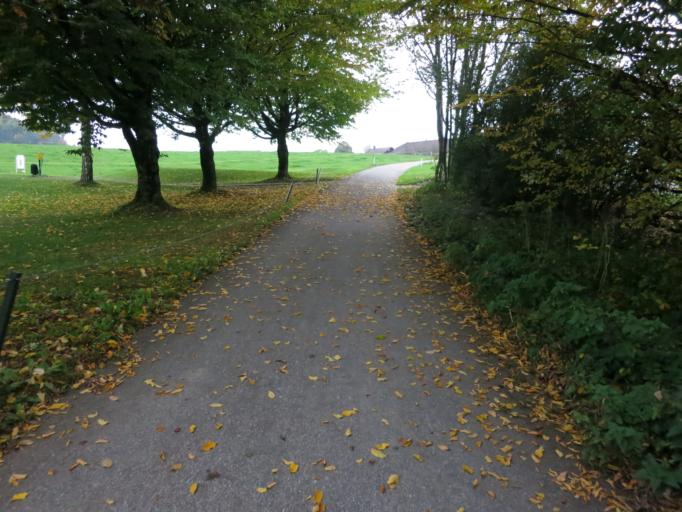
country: CH
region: Zurich
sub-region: Bezirk Hinwil
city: Bubikon
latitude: 47.2645
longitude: 8.8294
